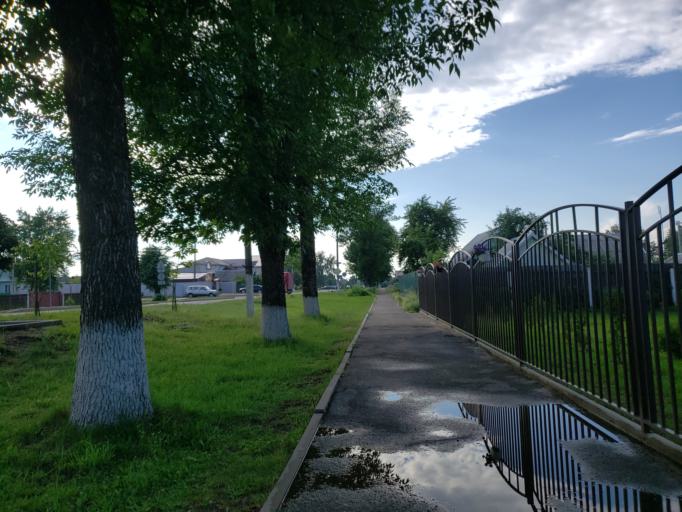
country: BY
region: Minsk
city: Chervyen'
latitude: 53.7046
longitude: 28.4376
